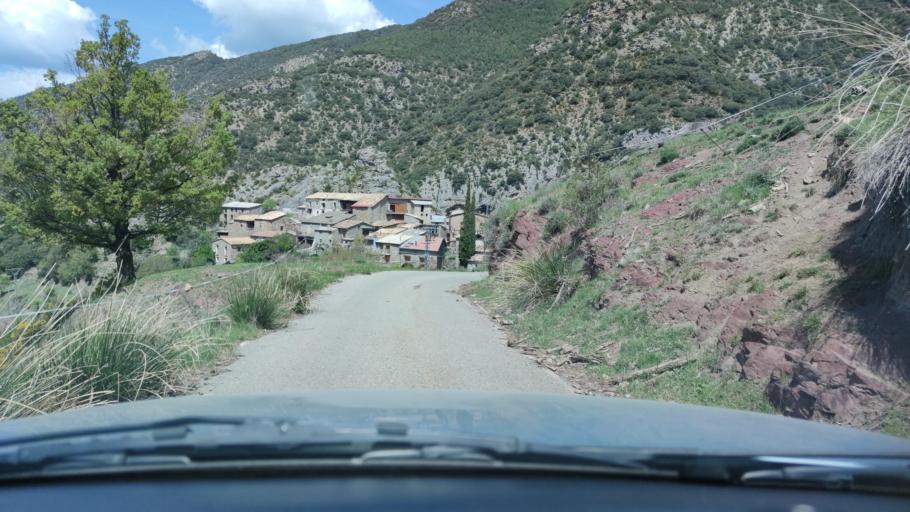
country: ES
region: Catalonia
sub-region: Provincia de Lleida
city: Sort
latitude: 42.3254
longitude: 1.1064
